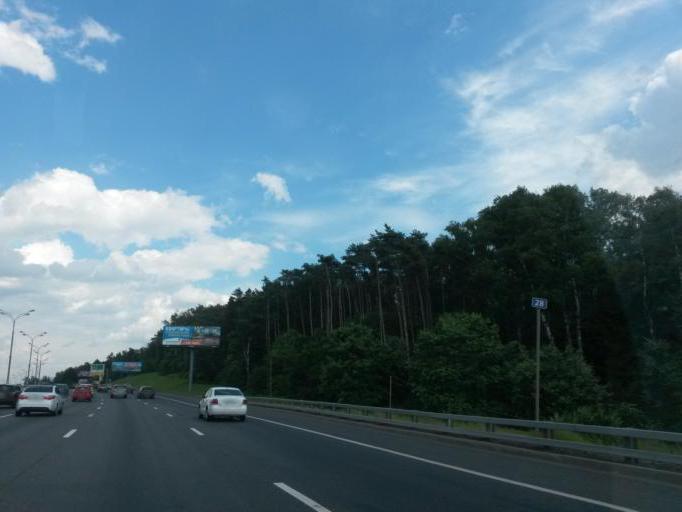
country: RU
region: Moscow
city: Zagor'ye
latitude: 55.5723
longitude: 37.6750
